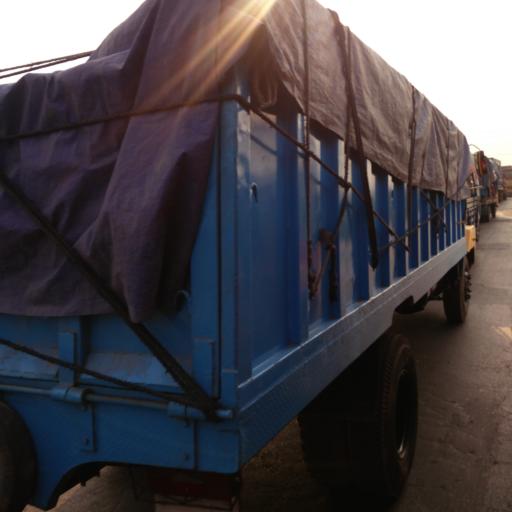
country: BD
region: Dhaka
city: Tungi
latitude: 23.8940
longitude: 90.3515
